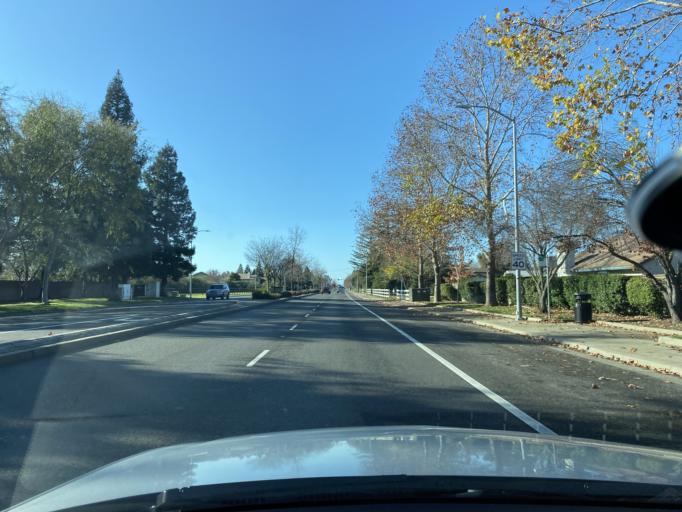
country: US
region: California
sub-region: Sacramento County
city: Elk Grove
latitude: 38.4381
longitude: -121.3803
